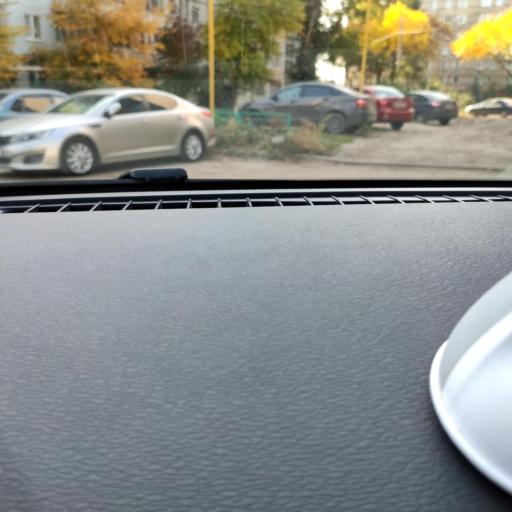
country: RU
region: Samara
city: Samara
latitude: 53.1881
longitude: 50.2166
